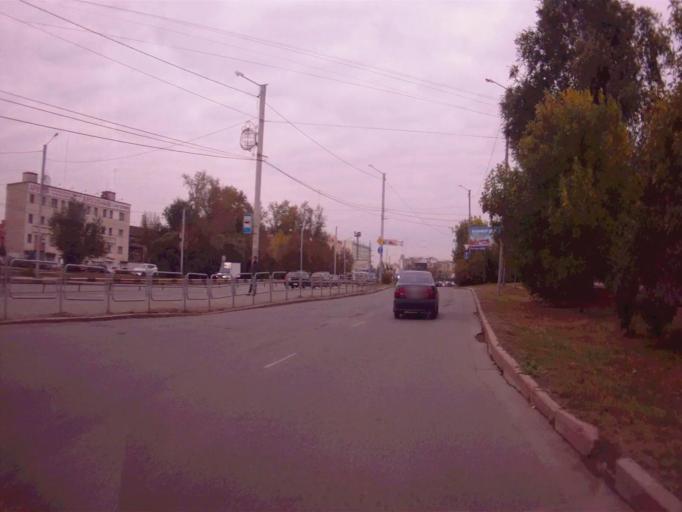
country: RU
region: Chelyabinsk
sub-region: Gorod Chelyabinsk
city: Chelyabinsk
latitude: 55.1376
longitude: 61.4093
